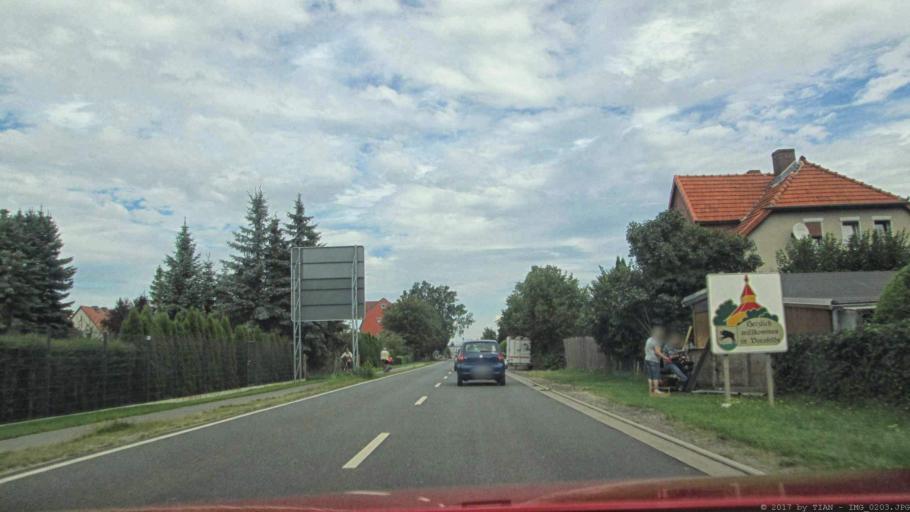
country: DE
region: Lower Saxony
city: Danndorf
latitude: 52.4275
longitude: 10.8478
